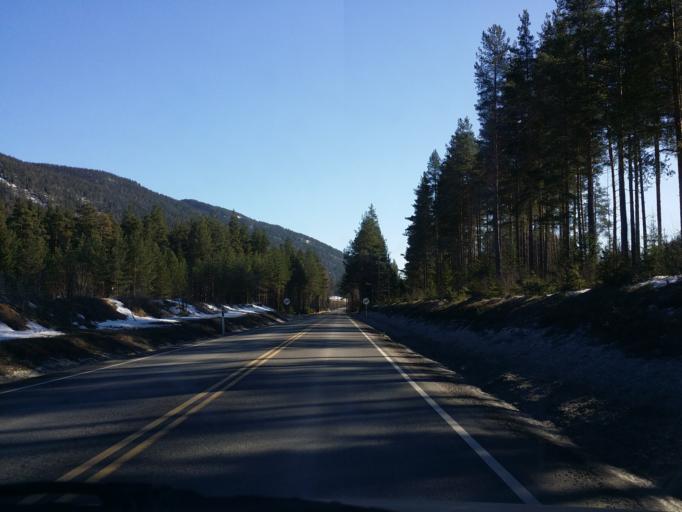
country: NO
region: Buskerud
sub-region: Ringerike
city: Honefoss
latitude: 60.3547
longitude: 10.0977
